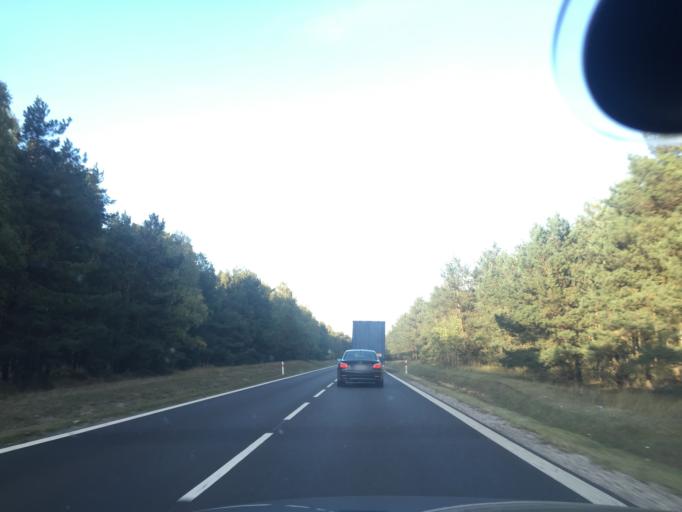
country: PL
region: Kujawsko-Pomorskie
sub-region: Powiat torunski
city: Wielka Nieszawka
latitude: 52.9494
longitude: 18.5263
